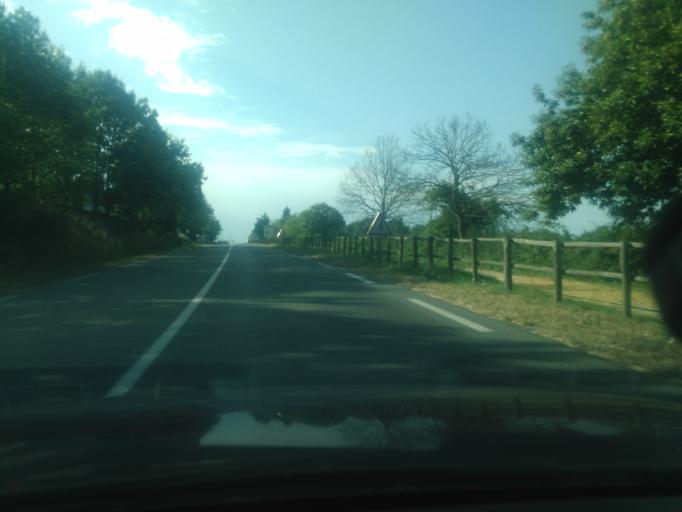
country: FR
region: Pays de la Loire
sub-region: Departement de la Vendee
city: Antigny
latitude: 46.6646
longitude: -0.7911
